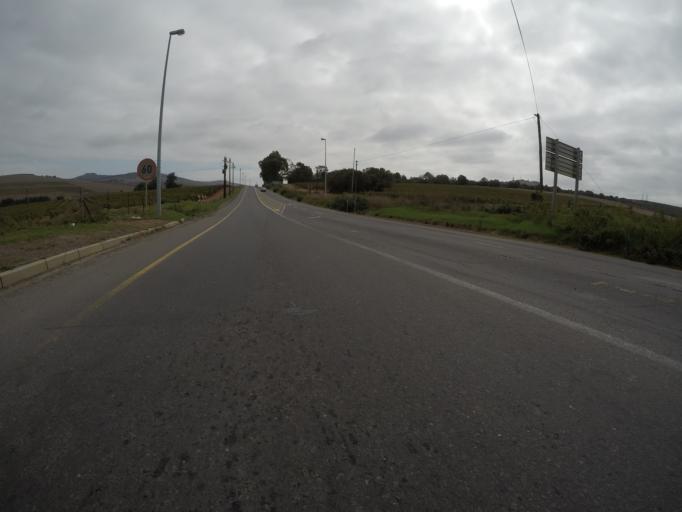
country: ZA
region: Western Cape
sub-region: City of Cape Town
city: Kraaifontein
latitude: -33.8427
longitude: 18.6237
